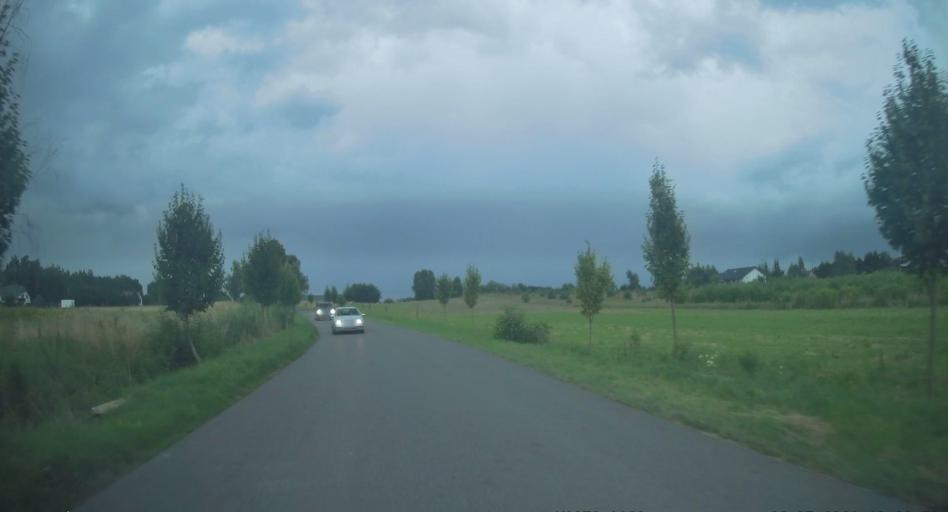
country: PL
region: Lodz Voivodeship
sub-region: Powiat rawski
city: Rawa Mazowiecka
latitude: 51.7464
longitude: 20.2089
